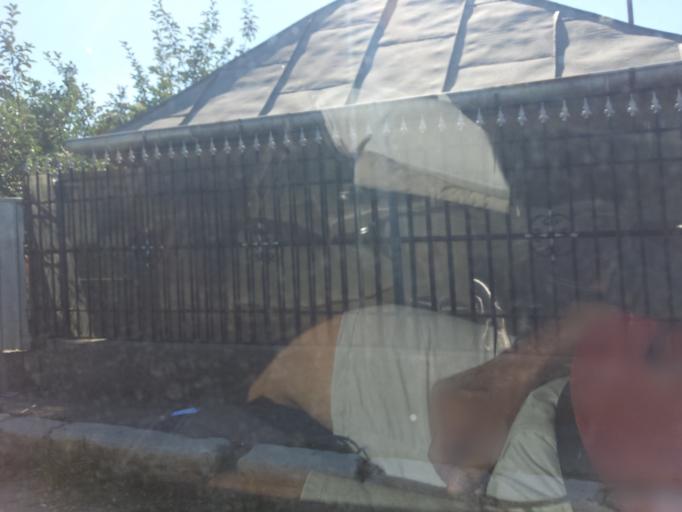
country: RO
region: Tulcea
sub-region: Municipiul Tulcea
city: Tulcea
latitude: 45.1849
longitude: 28.8153
